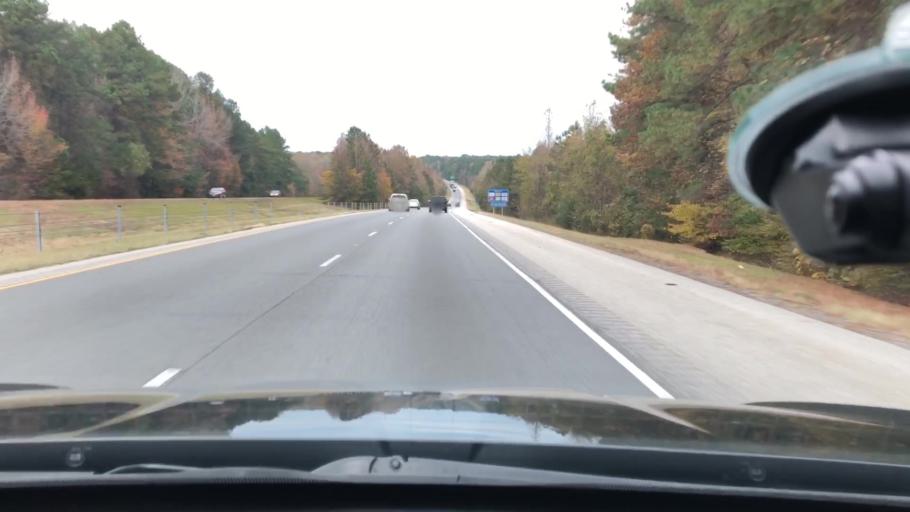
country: US
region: Arkansas
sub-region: Clark County
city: Arkadelphia
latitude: 34.0937
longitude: -93.1072
